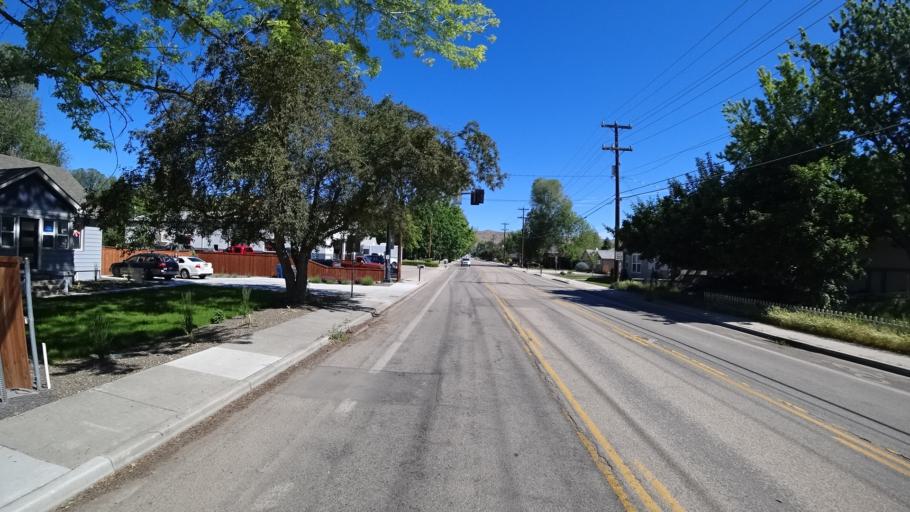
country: US
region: Idaho
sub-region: Ada County
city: Garden City
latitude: 43.6443
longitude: -116.2335
